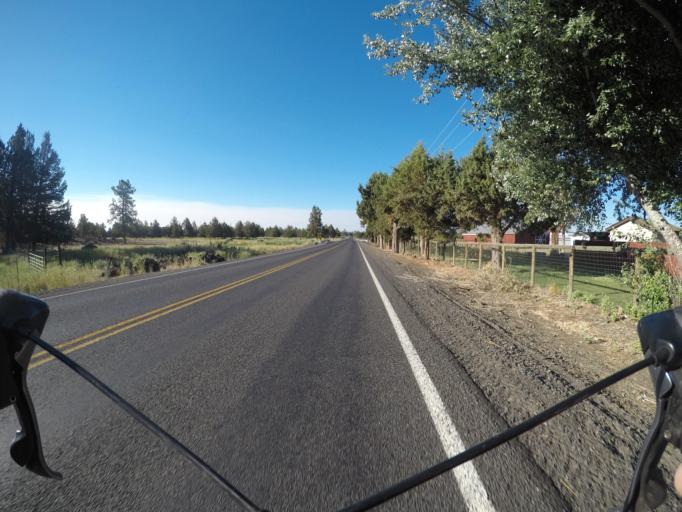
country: US
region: Oregon
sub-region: Deschutes County
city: Redmond
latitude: 44.2044
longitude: -121.2436
